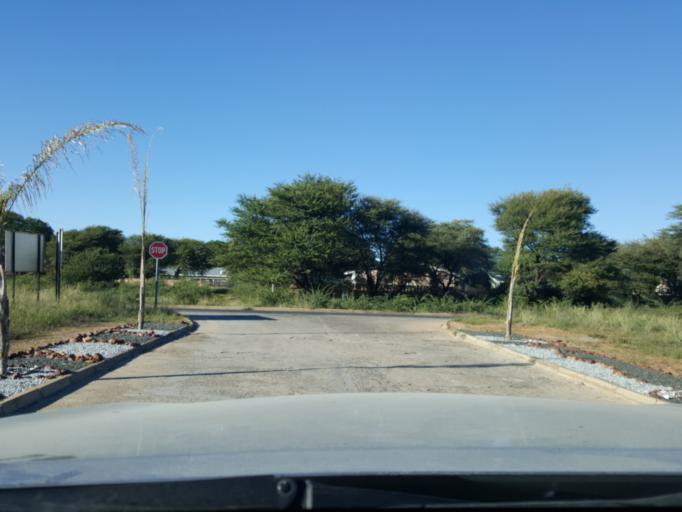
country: BW
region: Kweneng
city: Letlhakeng
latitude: -24.5930
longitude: 24.7256
